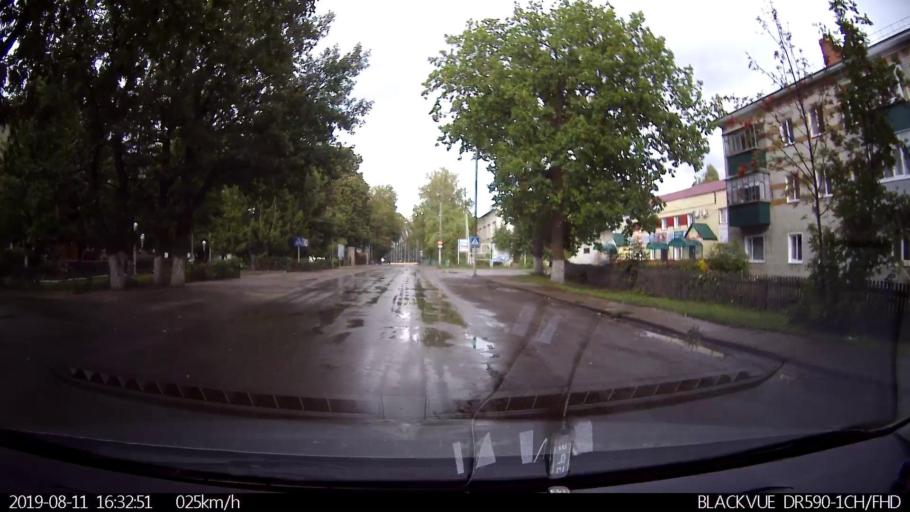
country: RU
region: Ulyanovsk
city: Mayna
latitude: 54.1132
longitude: 47.6241
